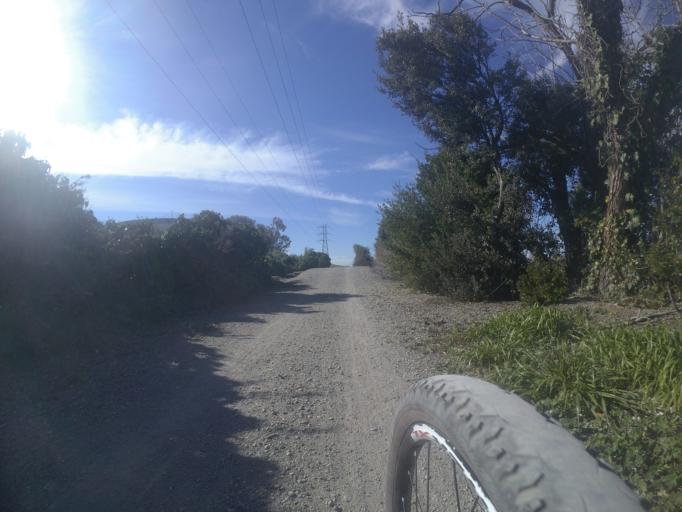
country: US
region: California
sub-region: Santa Clara County
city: Sunnyvale
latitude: 37.4200
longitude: -122.0163
